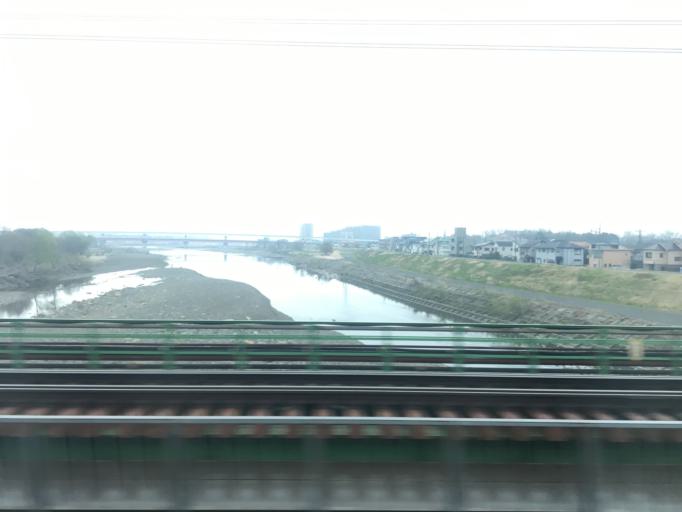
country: JP
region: Tokyo
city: Hino
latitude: 35.6855
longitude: 139.3971
